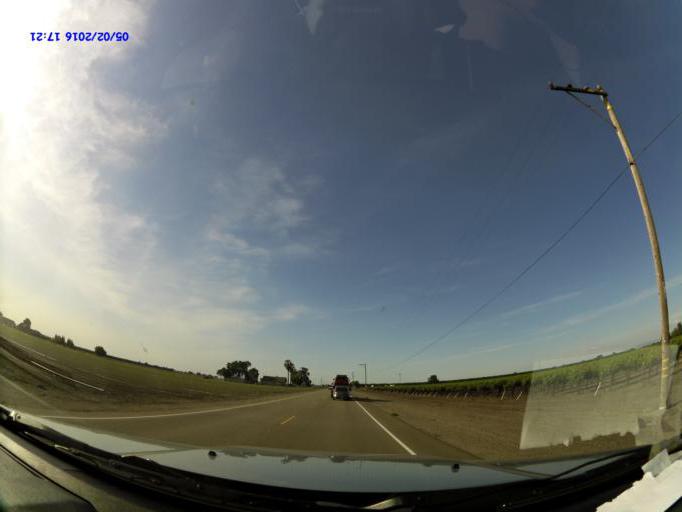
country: US
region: California
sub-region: San Joaquin County
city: Manteca
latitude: 37.8497
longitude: -121.1453
